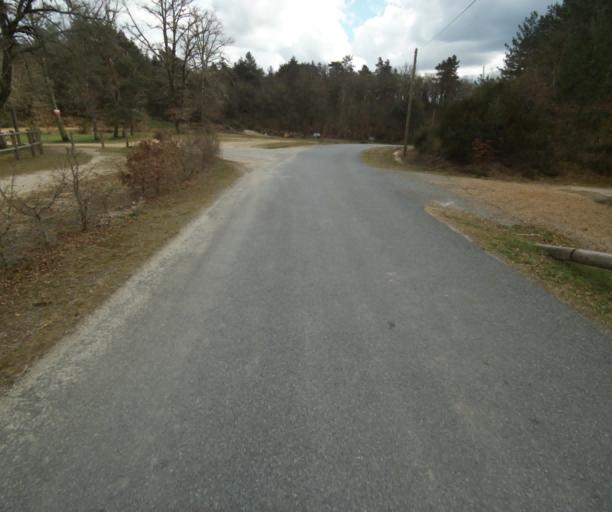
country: FR
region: Limousin
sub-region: Departement de la Correze
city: Correze
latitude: 45.3109
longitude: 1.9330
